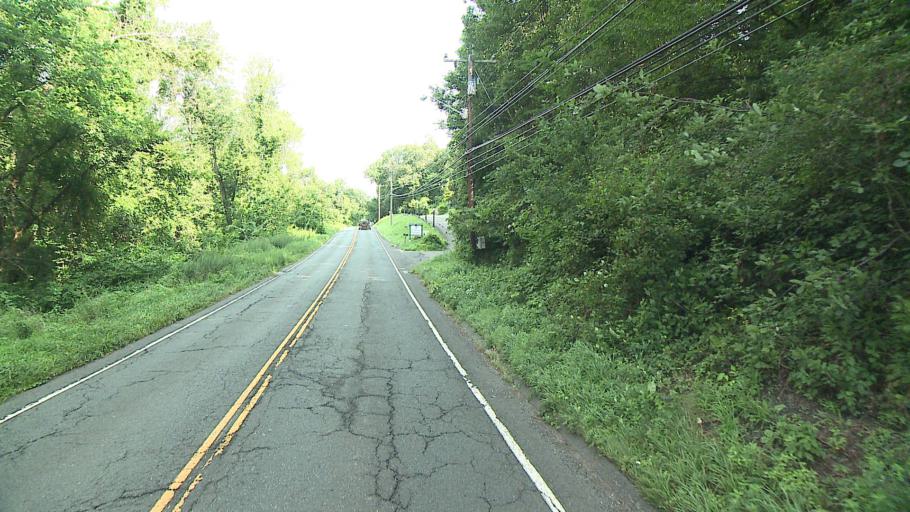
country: US
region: Connecticut
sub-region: Fairfield County
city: Danbury
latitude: 41.4522
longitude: -73.4746
